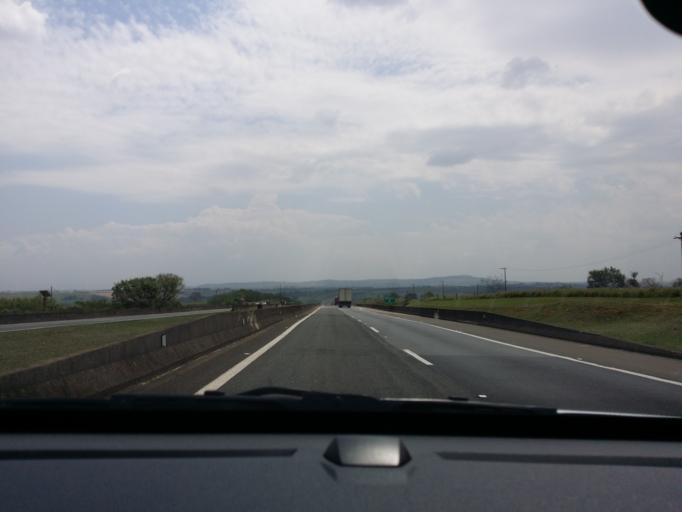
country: BR
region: Sao Paulo
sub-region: Iracemapolis
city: Iracemapolis
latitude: -22.6410
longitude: -47.4518
